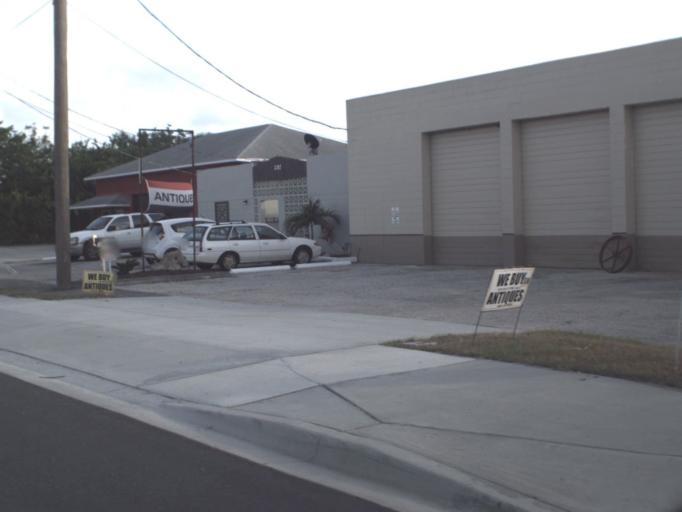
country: US
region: Florida
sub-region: Brevard County
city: Cocoa
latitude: 28.3922
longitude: -80.7479
